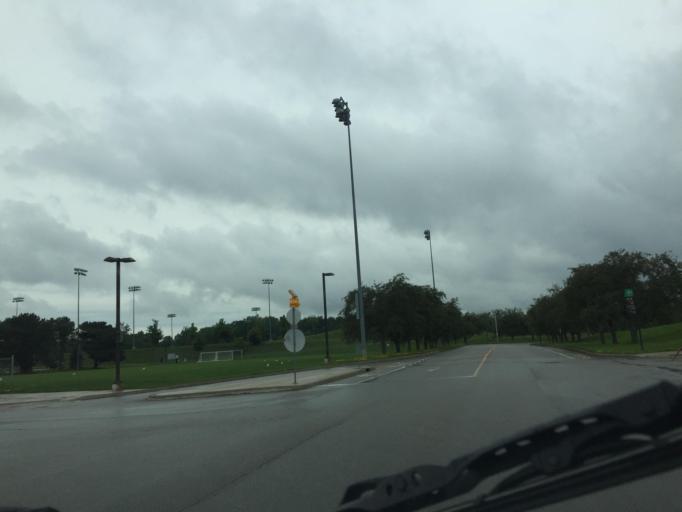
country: CA
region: Ontario
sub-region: Wellington County
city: Guelph
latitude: 43.5353
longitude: -80.2162
